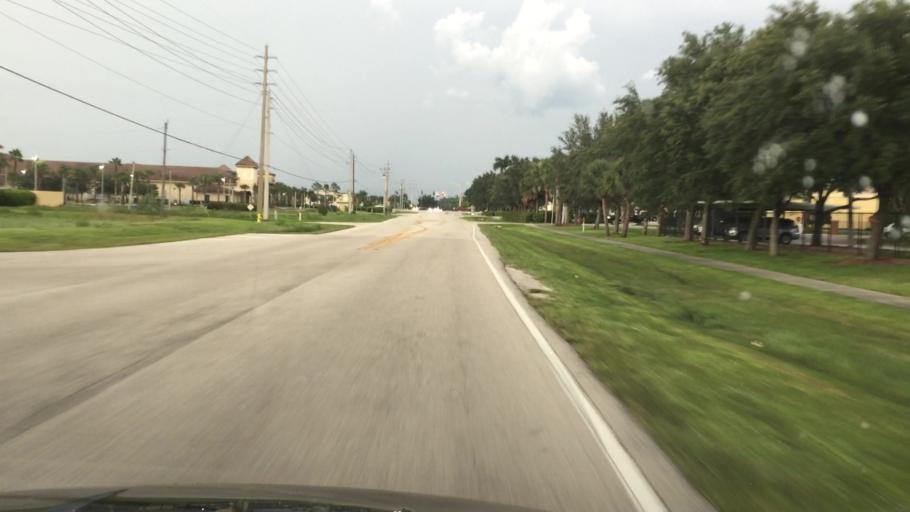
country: US
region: Florida
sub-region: Lee County
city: Villas
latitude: 26.5433
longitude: -81.8468
